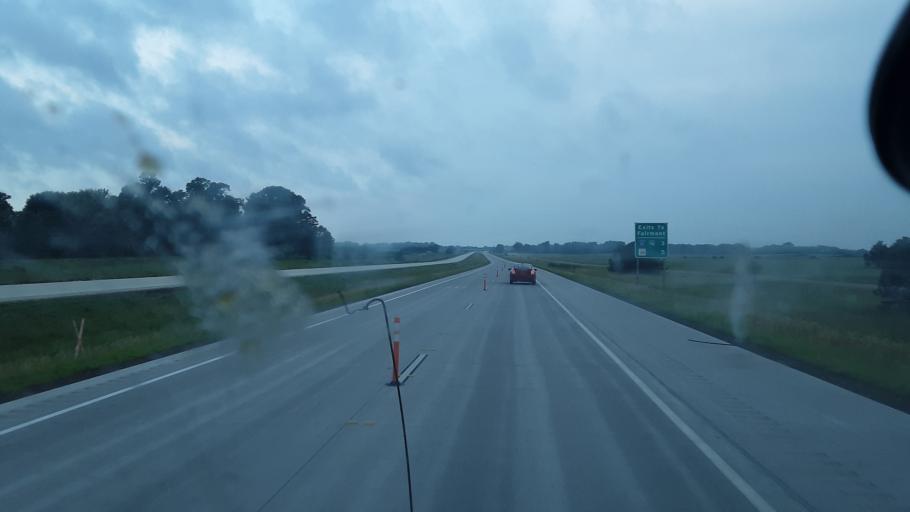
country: US
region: Minnesota
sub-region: Martin County
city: Fairmont
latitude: 43.6707
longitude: -94.3838
